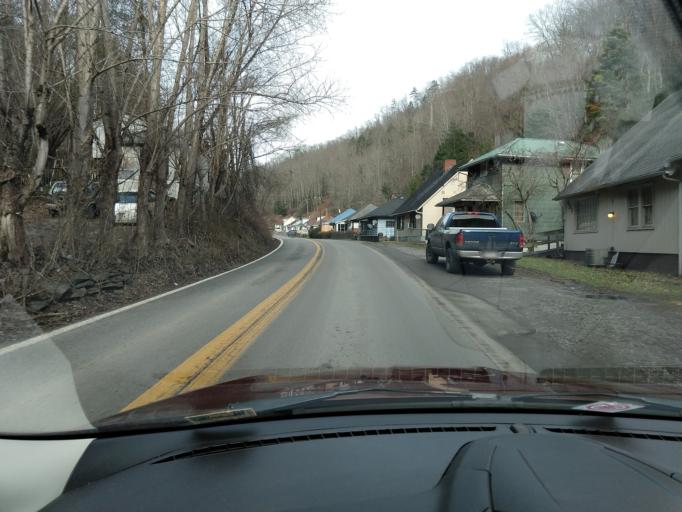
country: US
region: West Virginia
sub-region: McDowell County
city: Welch
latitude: 37.3351
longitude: -81.6737
